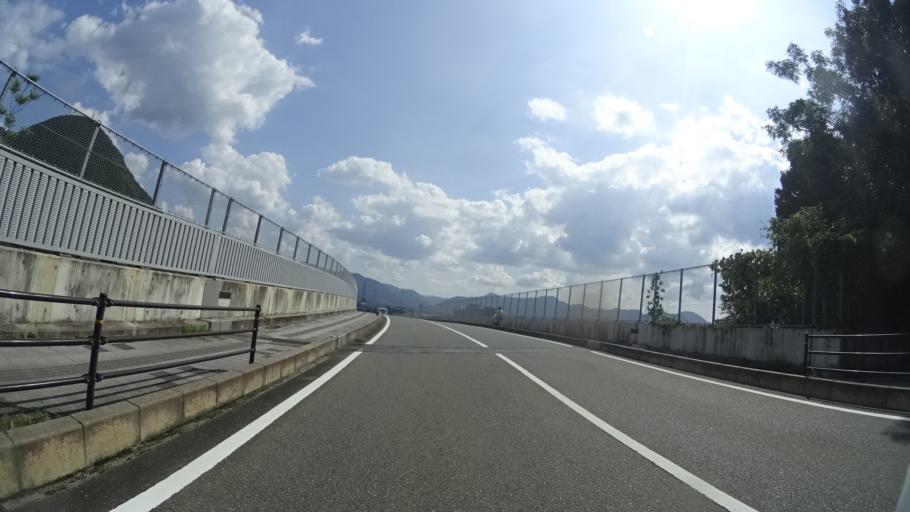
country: JP
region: Yamaguchi
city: Hagi
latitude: 34.4242
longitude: 131.4126
